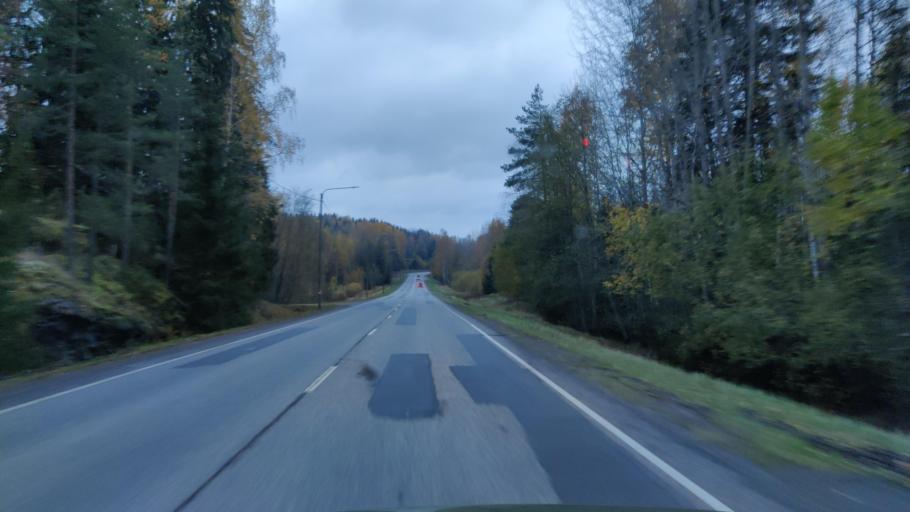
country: FI
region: Uusimaa
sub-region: Helsinki
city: Vihti
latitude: 60.3224
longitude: 24.2203
